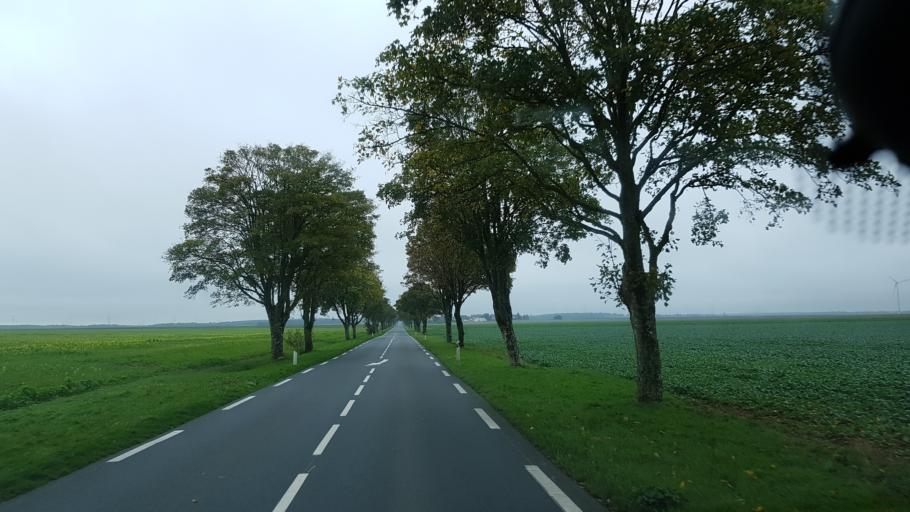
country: FR
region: Ile-de-France
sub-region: Departement de l'Essonne
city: Pussay
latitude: 48.3879
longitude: 1.9747
